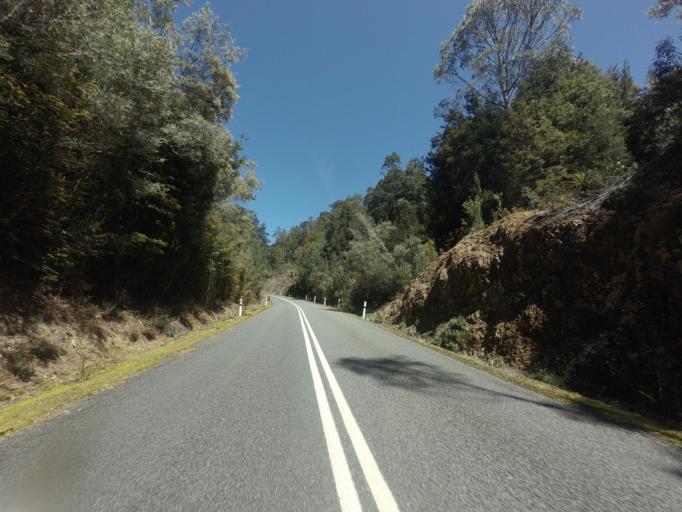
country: AU
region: Tasmania
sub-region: Huon Valley
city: Geeveston
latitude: -42.8148
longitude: 146.3685
